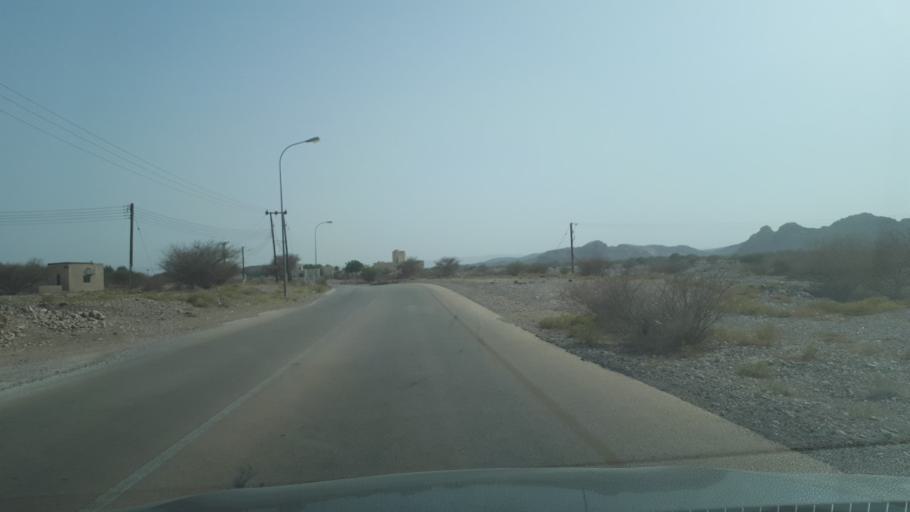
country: OM
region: Az Zahirah
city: `Ibri
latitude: 23.1645
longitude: 56.9146
